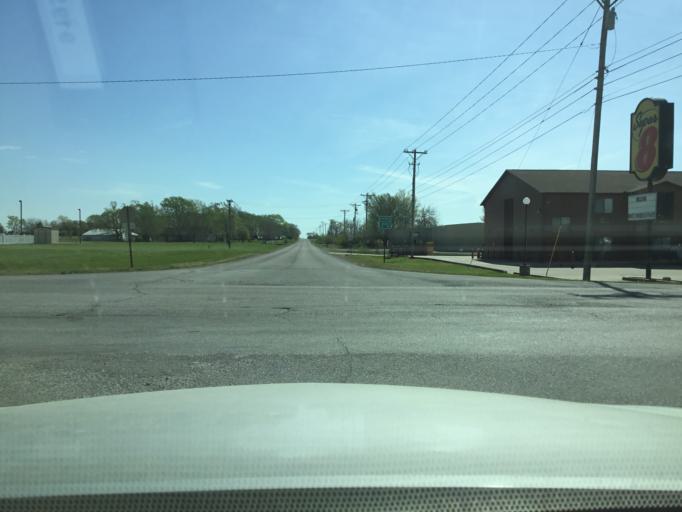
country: US
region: Kansas
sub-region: Neosho County
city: Chanute
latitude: 37.6458
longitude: -95.4528
